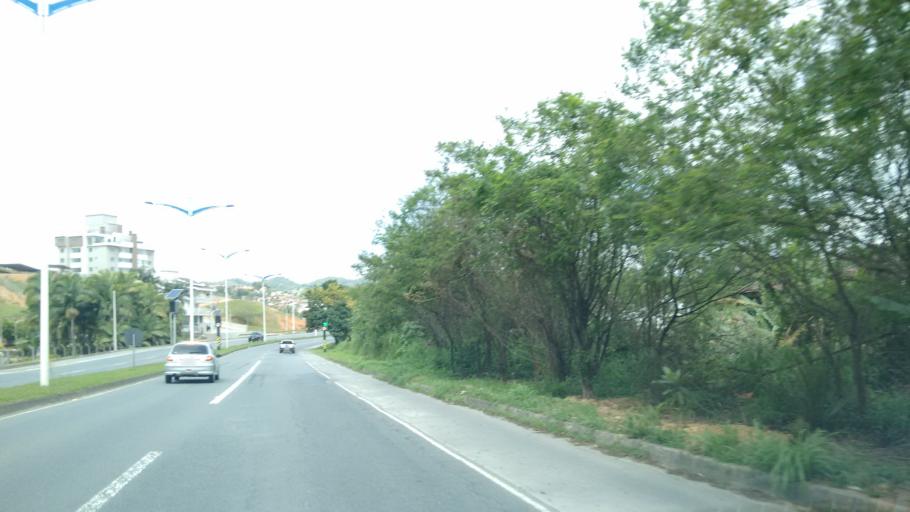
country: BR
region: Santa Catarina
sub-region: Blumenau
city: Blumenau
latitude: -26.8733
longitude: -49.0686
